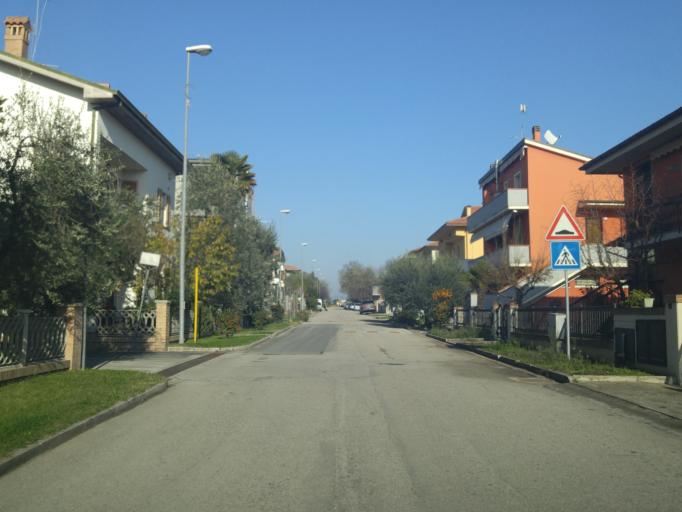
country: IT
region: The Marches
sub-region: Provincia di Pesaro e Urbino
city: Calcinelli
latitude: 43.7619
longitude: 12.9261
